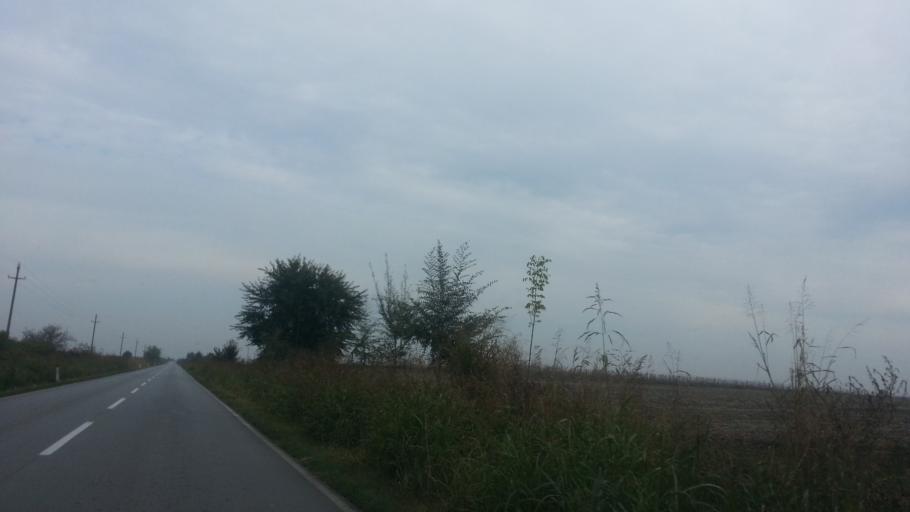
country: RS
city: Belegis
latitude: 45.0319
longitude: 20.3343
